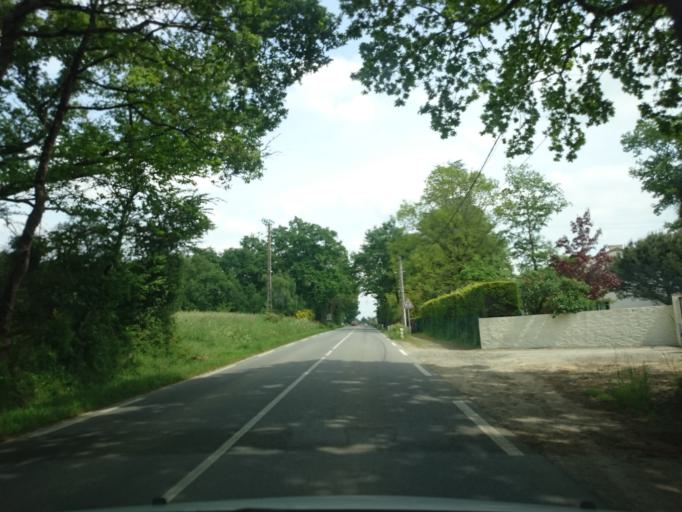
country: FR
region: Pays de la Loire
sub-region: Departement de la Loire-Atlantique
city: Pont-Saint-Martin
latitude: 47.1247
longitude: -1.6004
